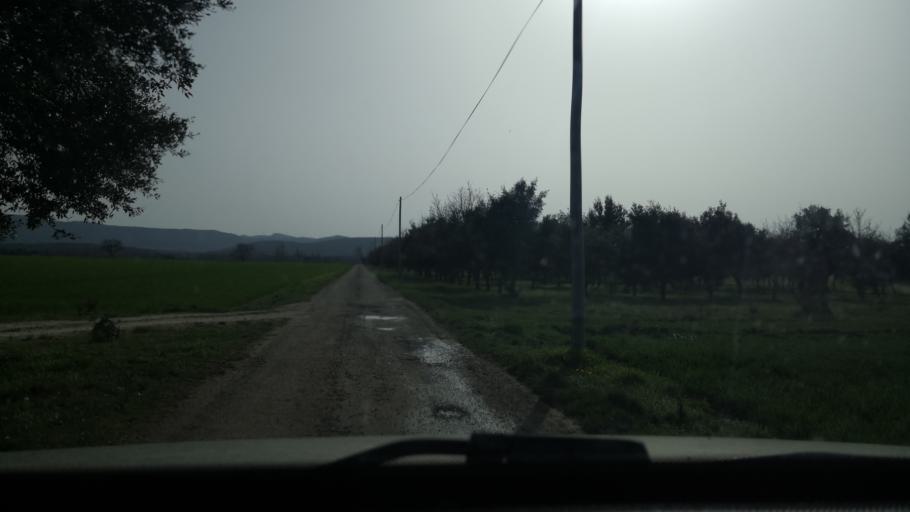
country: FR
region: Rhone-Alpes
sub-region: Departement de la Drome
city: La Begude-de-Mazenc
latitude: 44.5585
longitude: 4.8967
